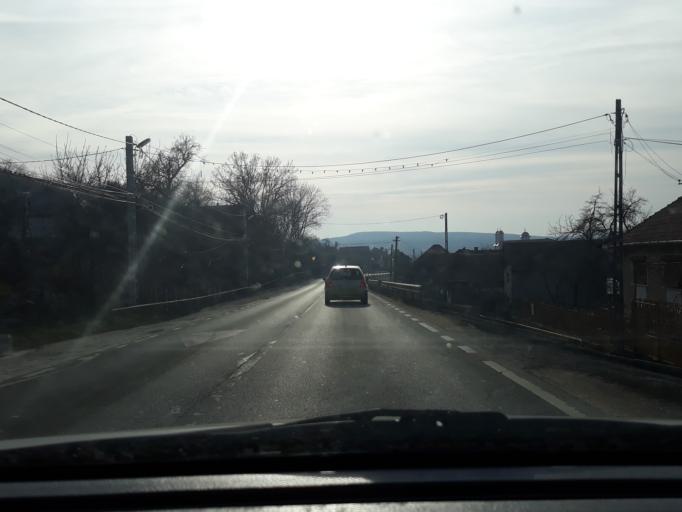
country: RO
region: Salaj
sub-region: Comuna Criseni
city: Criseni
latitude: 47.2341
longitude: 23.0490
